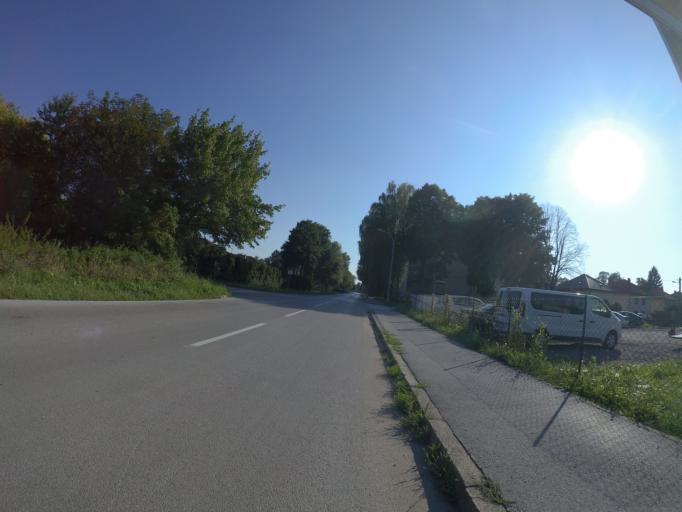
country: HR
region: Karlovacka
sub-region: Grad Karlovac
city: Karlovac
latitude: 45.5007
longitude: 15.5613
